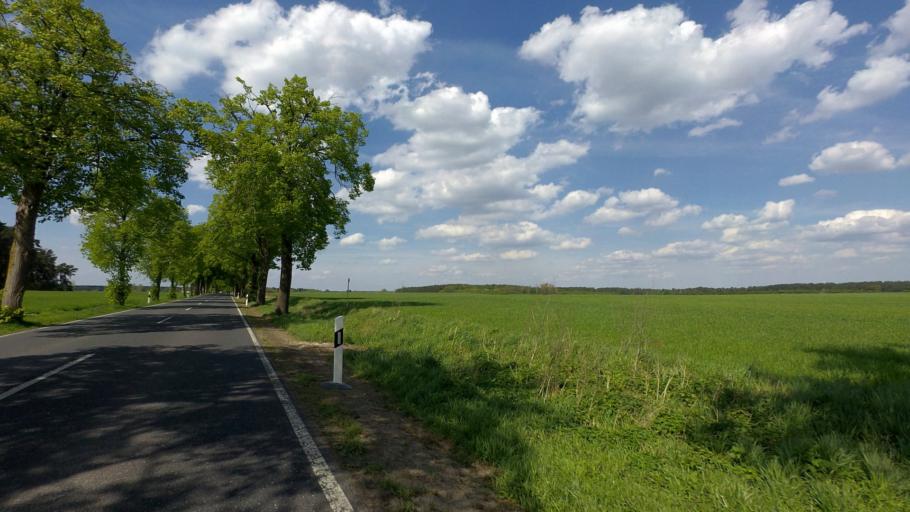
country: DE
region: Brandenburg
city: Marienwerder
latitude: 52.8903
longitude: 13.5433
